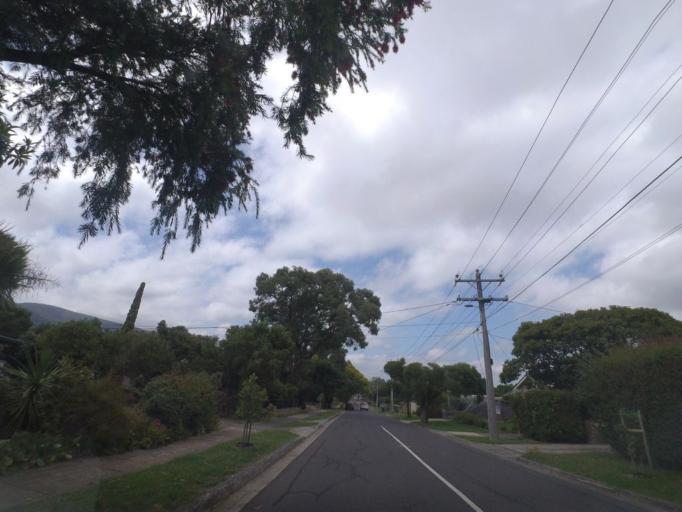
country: AU
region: Victoria
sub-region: Knox
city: Boronia
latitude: -37.8654
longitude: 145.2776
